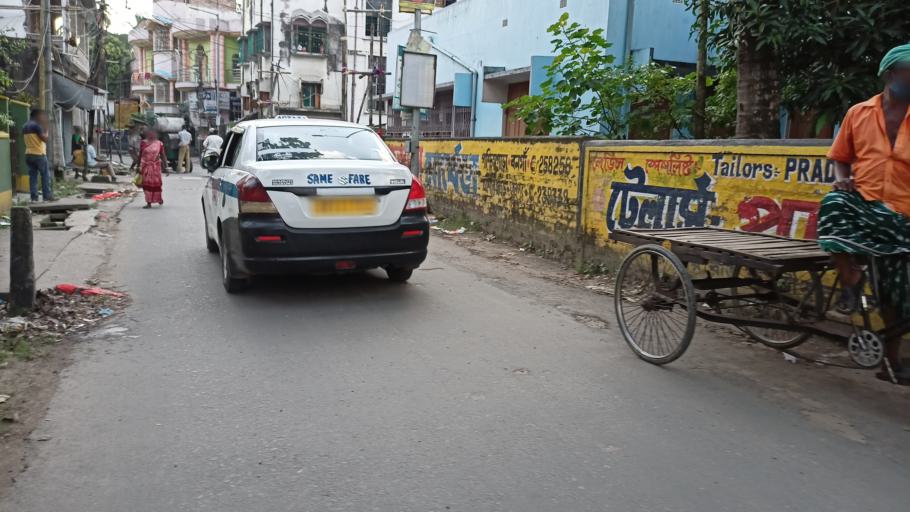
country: IN
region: West Bengal
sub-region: North 24 Parganas
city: Bangaon
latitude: 23.0451
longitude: 88.8261
